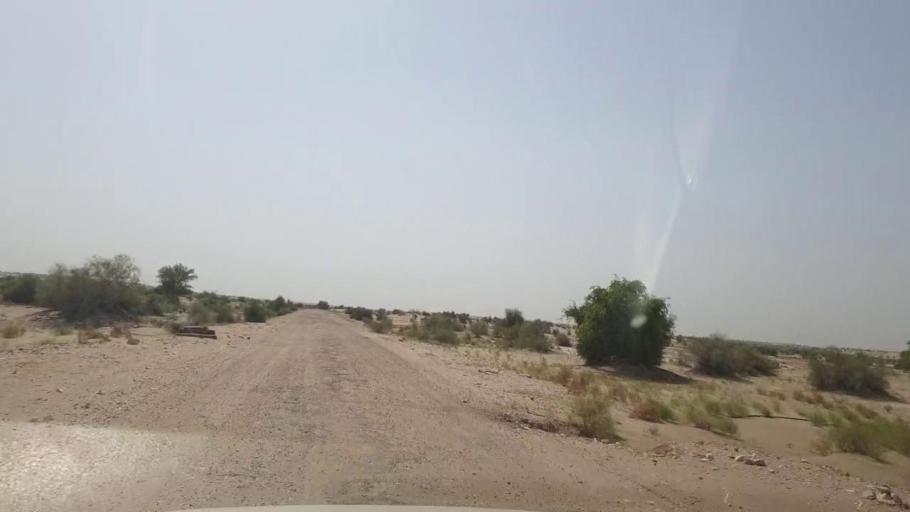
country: PK
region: Sindh
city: Khanpur
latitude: 27.4308
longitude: 69.2542
